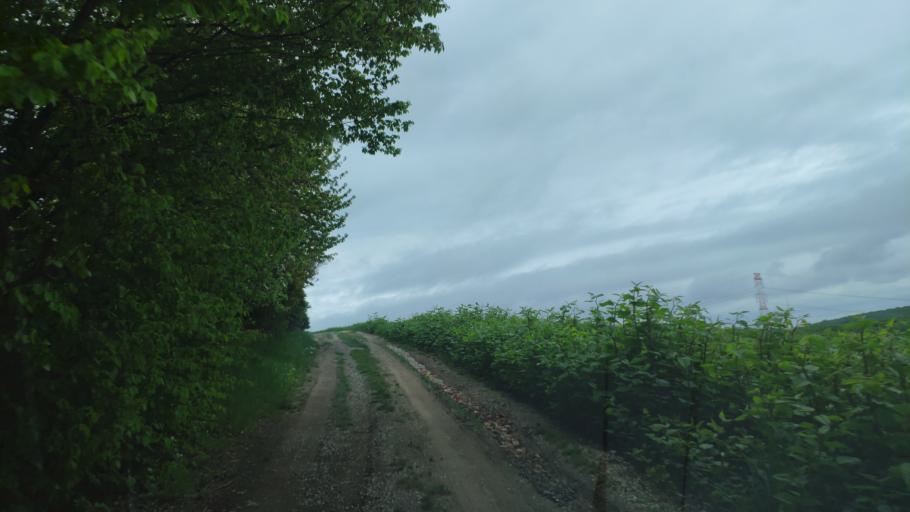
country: SK
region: Kosicky
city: Kosice
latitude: 48.7586
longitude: 21.1990
